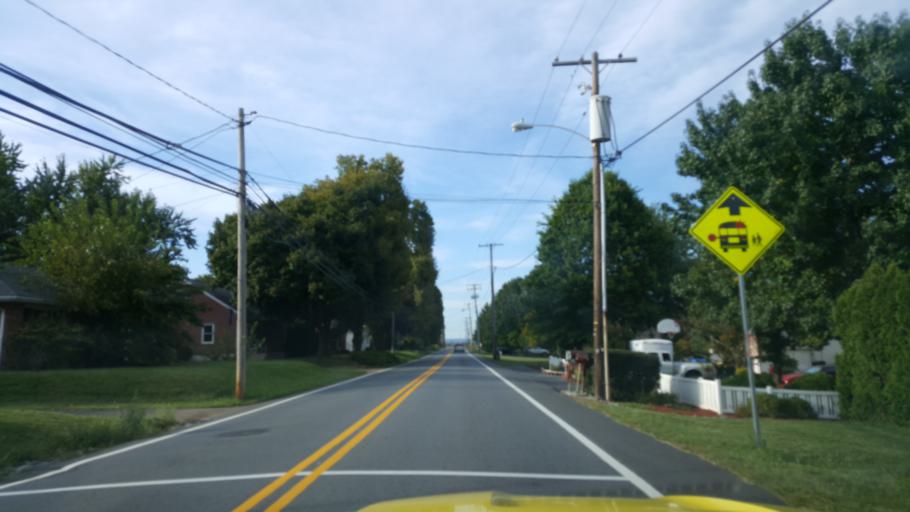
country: US
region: Pennsylvania
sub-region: Lebanon County
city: Campbelltown
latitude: 40.2747
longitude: -76.5692
